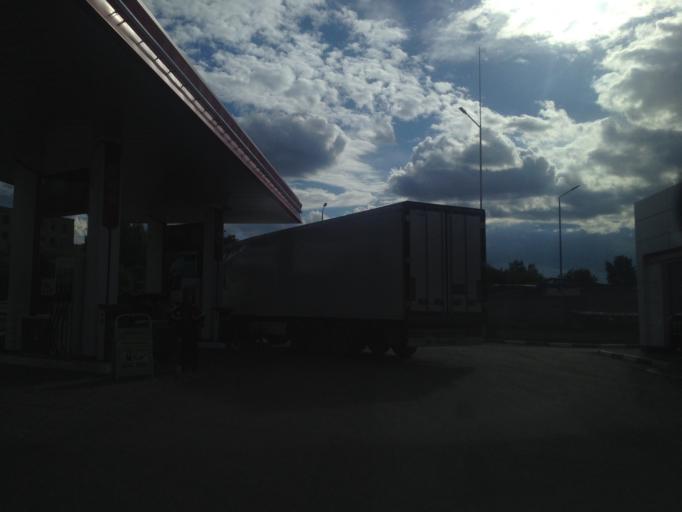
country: RU
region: Sverdlovsk
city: Yekaterinburg
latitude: 56.8689
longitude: 60.5857
